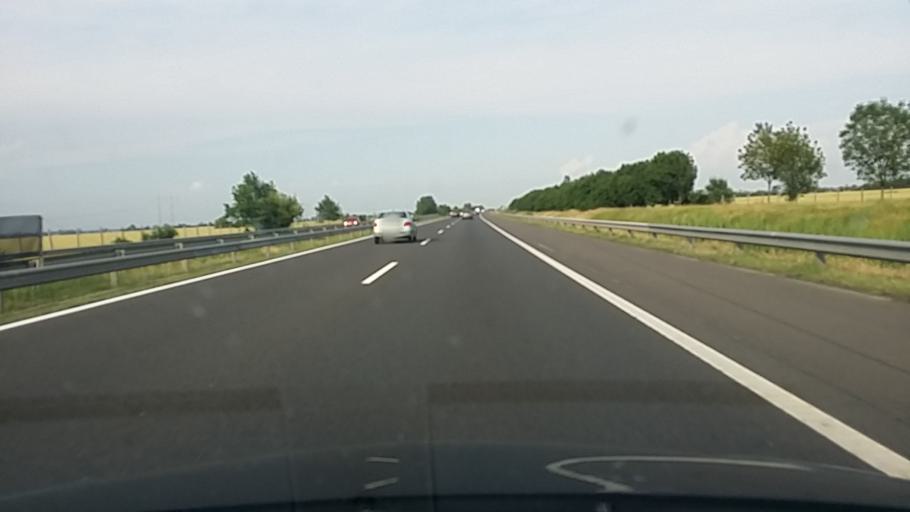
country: HU
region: Heves
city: Kompolt
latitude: 47.7096
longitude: 20.1897
